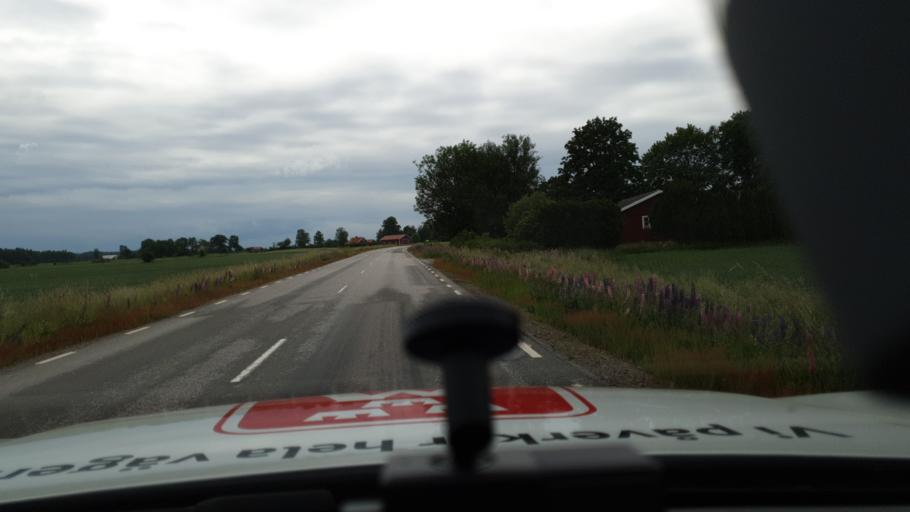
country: SE
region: Vaestra Goetaland
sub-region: Mariestads Kommun
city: Mariestad
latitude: 58.6466
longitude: 13.9013
